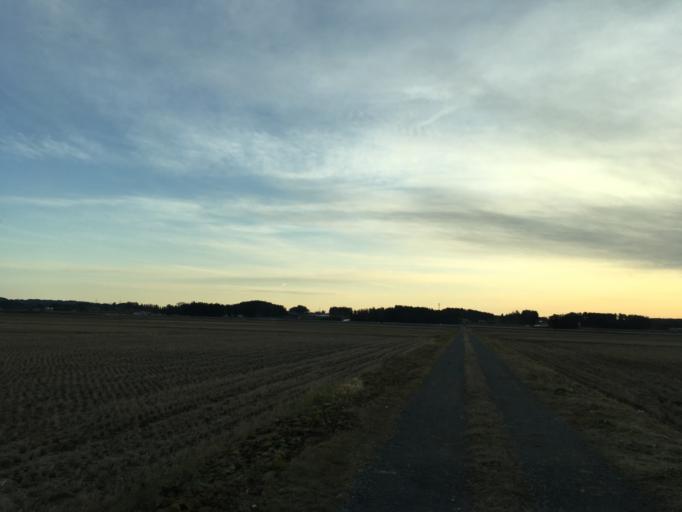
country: JP
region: Miyagi
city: Kogota
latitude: 38.6482
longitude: 141.0644
